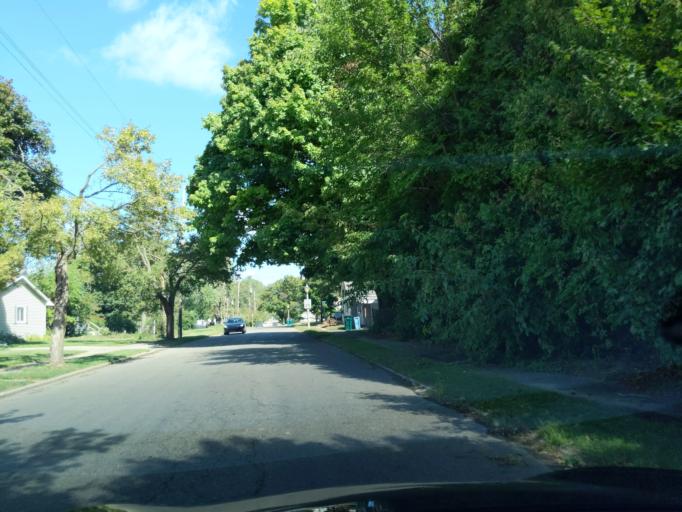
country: US
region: Michigan
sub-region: Ingham County
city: Lansing
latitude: 42.6909
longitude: -84.5528
